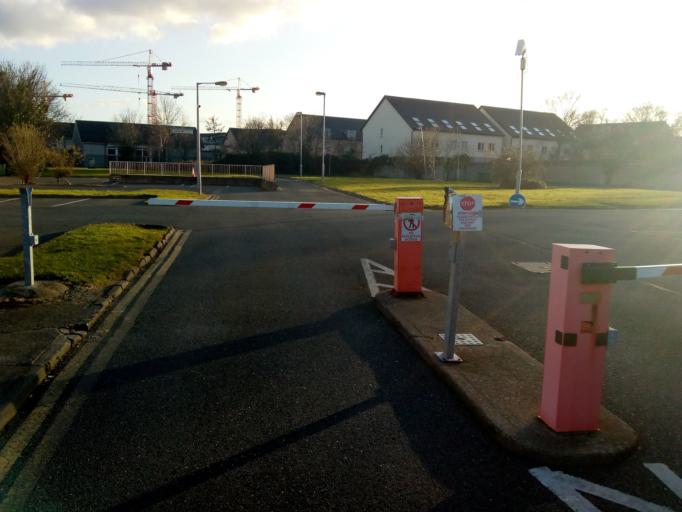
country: IE
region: Leinster
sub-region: Dun Laoghaire-Rathdown
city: Dun Laoghaire
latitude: 53.2879
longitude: -6.1395
